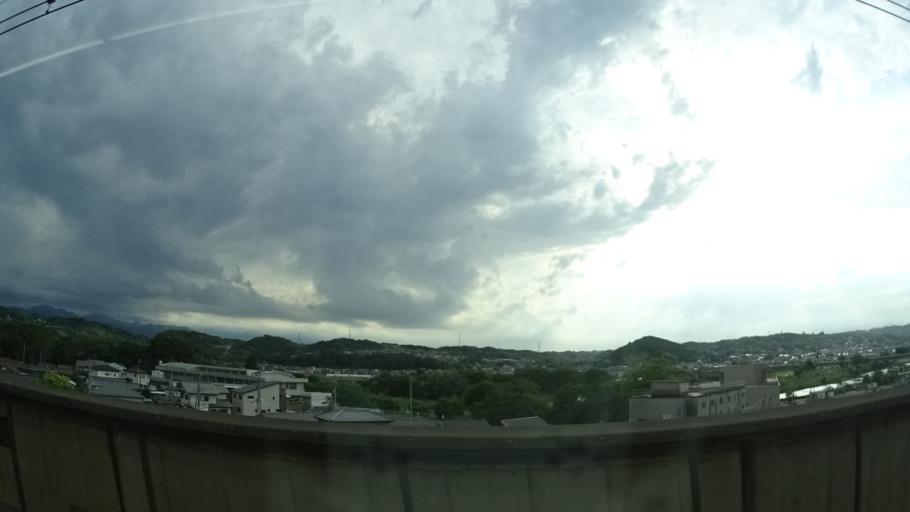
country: JP
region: Gunma
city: Takasaki
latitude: 36.3068
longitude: 139.0165
